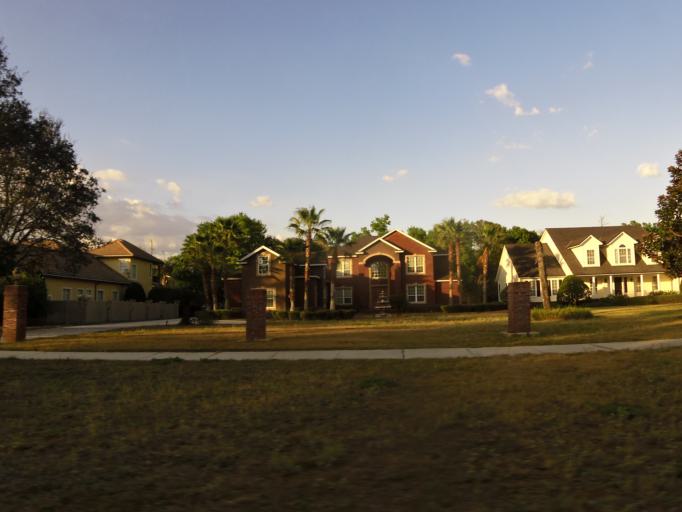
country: US
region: Florida
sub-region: Saint Johns County
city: Fruit Cove
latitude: 30.1228
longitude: -81.5810
